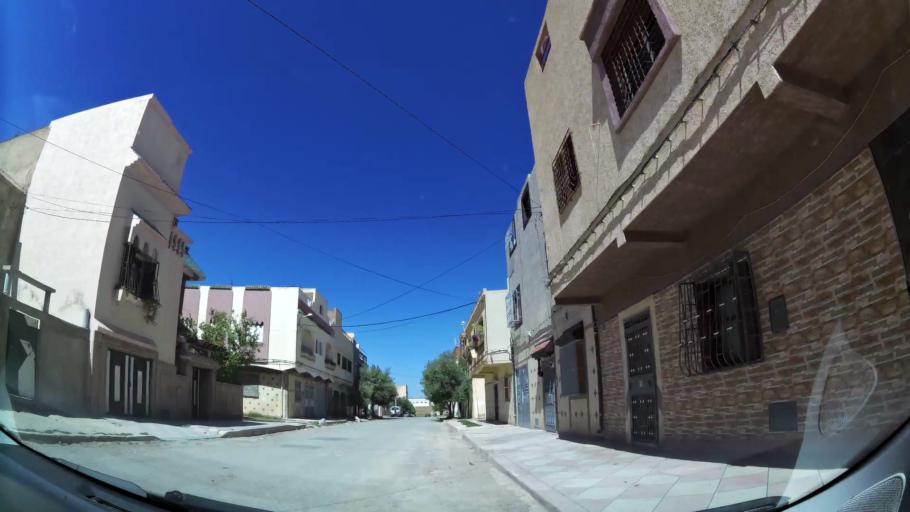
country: MA
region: Oriental
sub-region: Oujda-Angad
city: Oujda
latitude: 34.6646
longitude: -1.8707
